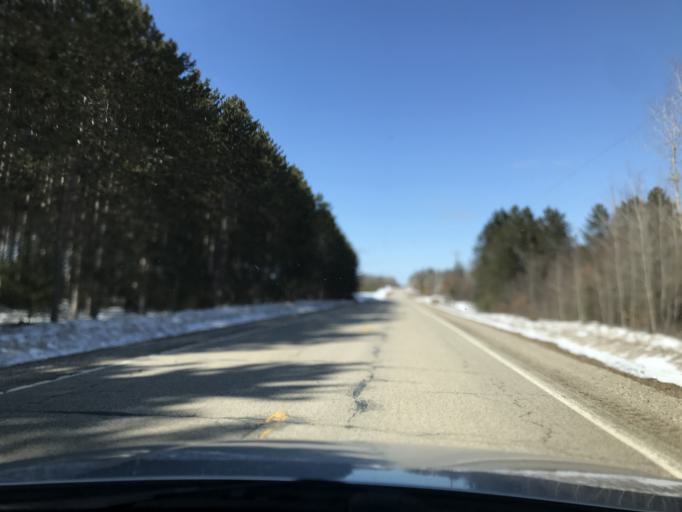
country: US
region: Wisconsin
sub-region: Marinette County
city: Niagara
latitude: 45.3459
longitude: -88.1014
